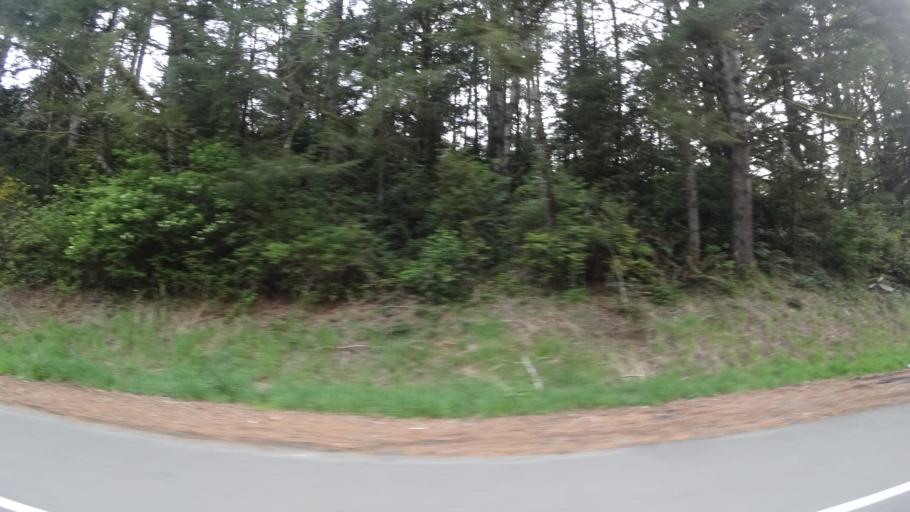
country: US
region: Oregon
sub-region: Coos County
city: Barview
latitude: 43.2548
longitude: -124.2800
